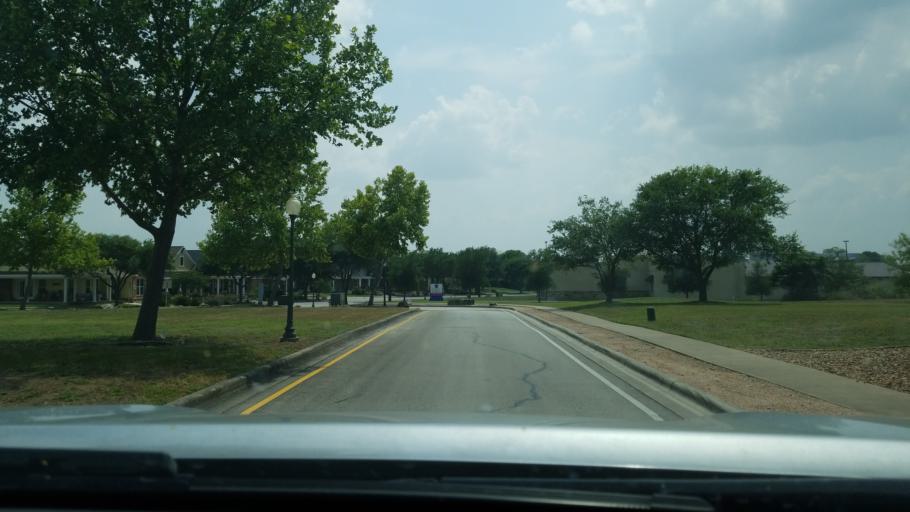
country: US
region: Texas
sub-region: Comal County
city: New Braunfels
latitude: 29.7283
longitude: -98.1003
